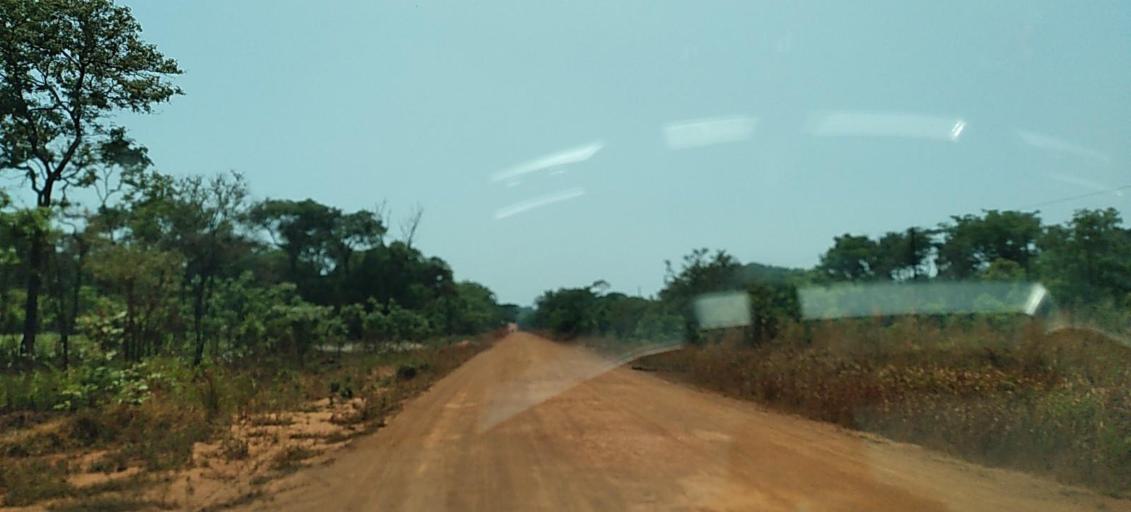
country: ZM
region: North-Western
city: Kansanshi
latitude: -11.9876
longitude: 26.8469
